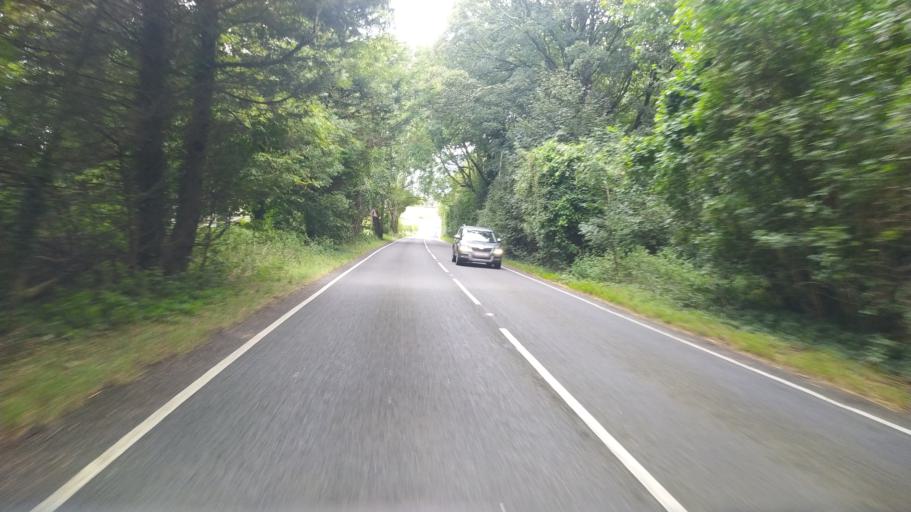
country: GB
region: England
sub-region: Dorset
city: Blandford Forum
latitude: 50.9121
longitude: -2.0607
